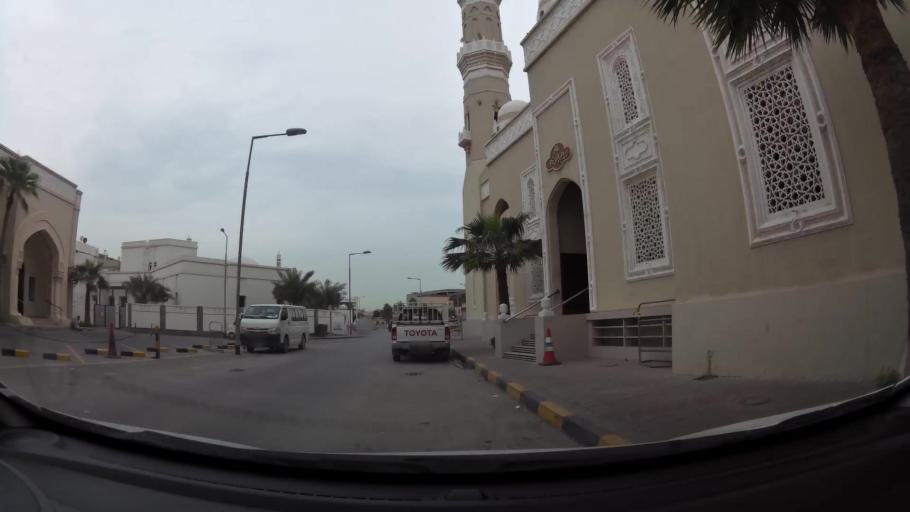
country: BH
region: Manama
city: Manama
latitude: 26.2194
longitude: 50.5662
